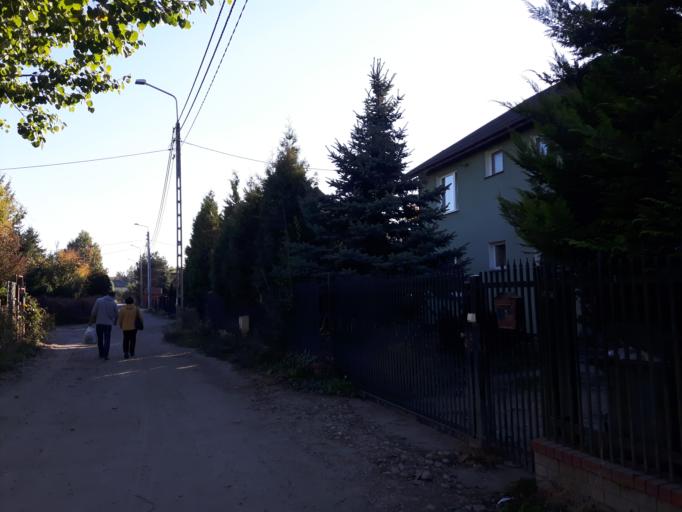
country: PL
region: Masovian Voivodeship
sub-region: Powiat wolominski
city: Zabki
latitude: 52.2840
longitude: 21.1320
